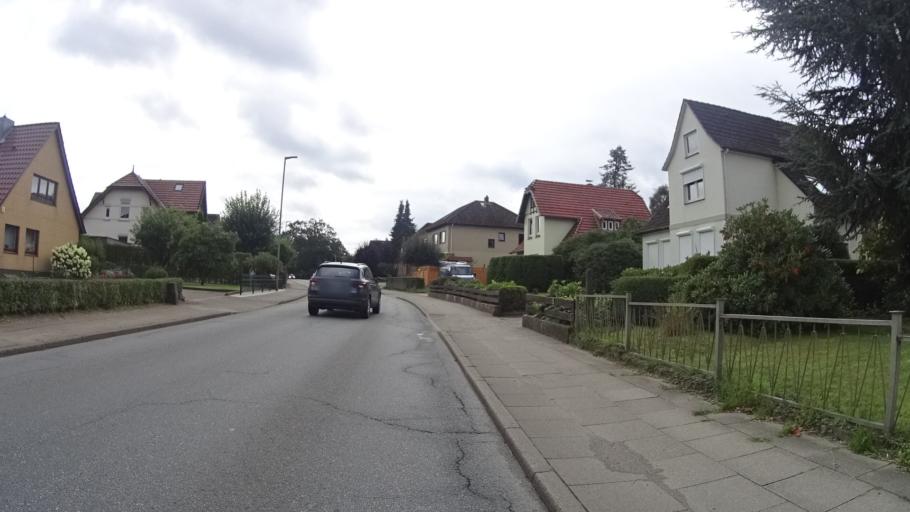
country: DE
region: Schleswig-Holstein
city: Tangstedt
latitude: 53.7442
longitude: 10.0679
